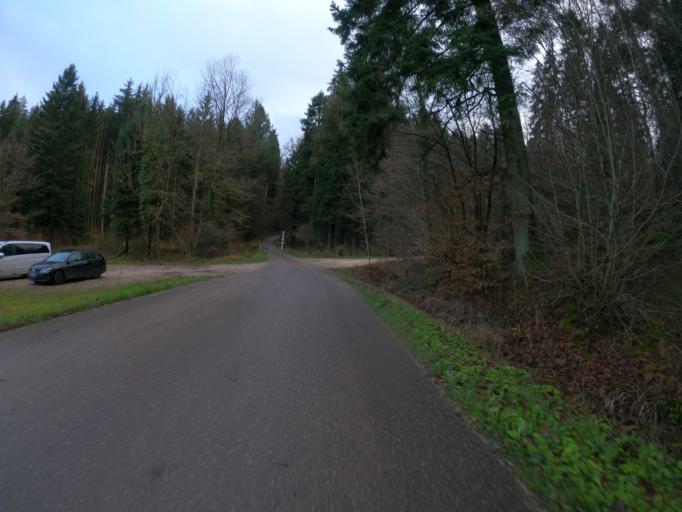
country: DE
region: Baden-Wuerttemberg
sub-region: Regierungsbezirk Stuttgart
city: Lorch
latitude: 48.7887
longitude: 9.7228
